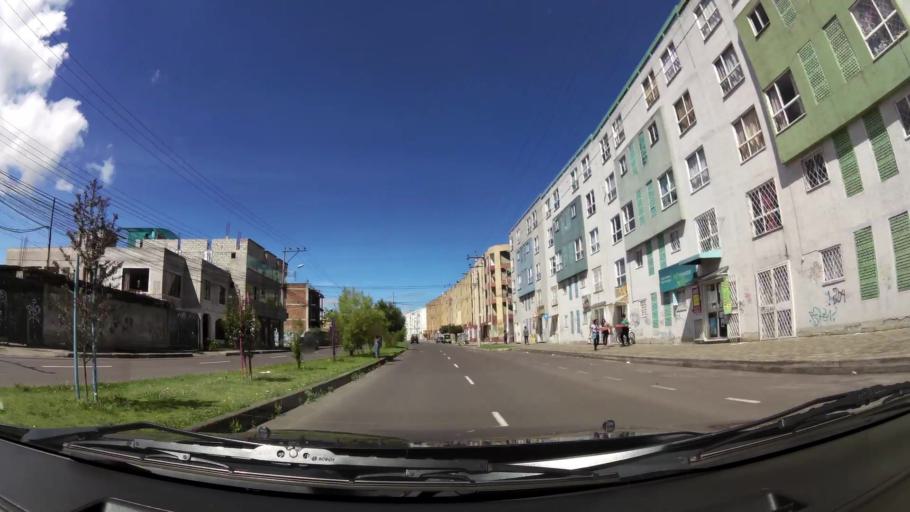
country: EC
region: Pichincha
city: Quito
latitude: -0.2963
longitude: -78.5466
